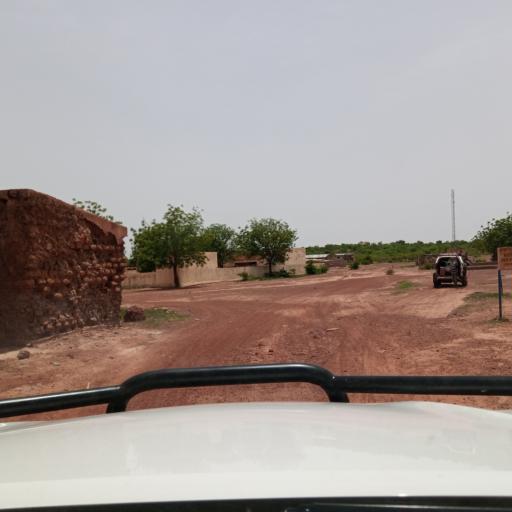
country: ML
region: Koulikoro
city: Koulikoro
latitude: 13.1073
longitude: -7.6099
